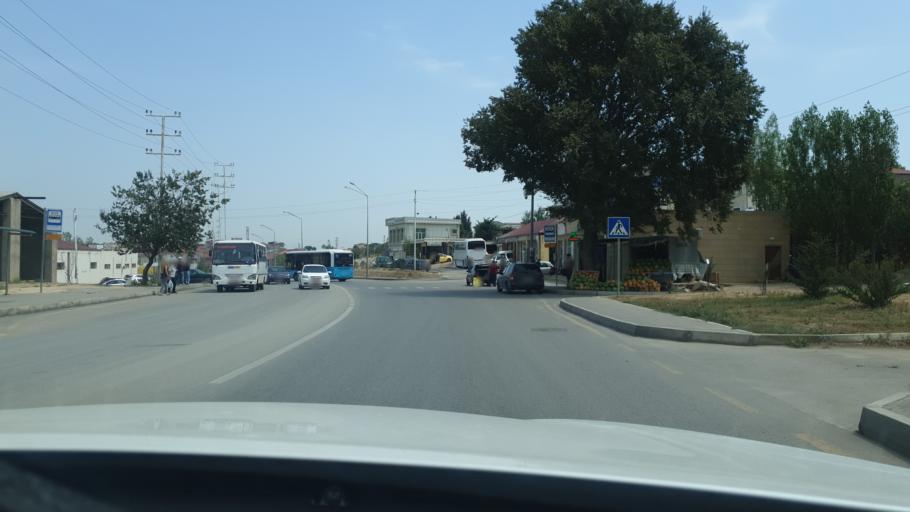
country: AZ
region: Baki
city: Qaracuxur
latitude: 40.3925
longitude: 49.9807
